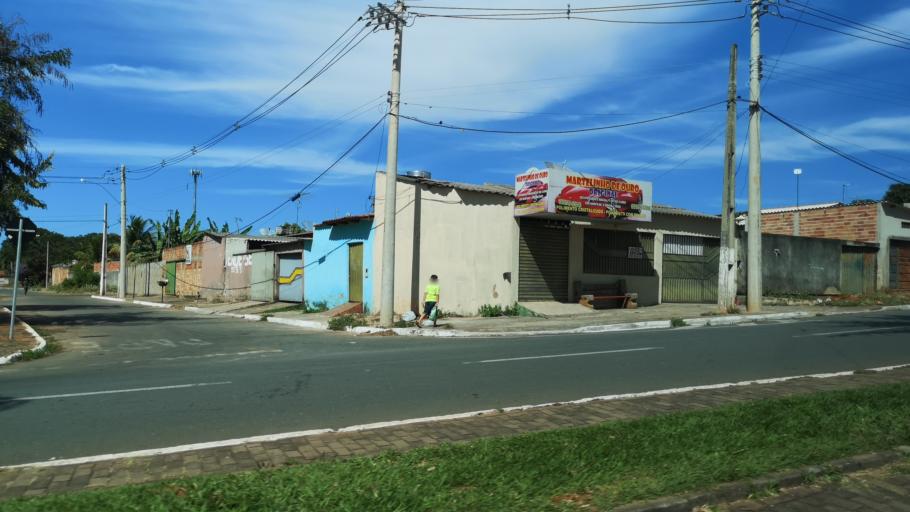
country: BR
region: Goias
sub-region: Senador Canedo
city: Senador Canedo
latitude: -16.6923
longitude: -49.0972
